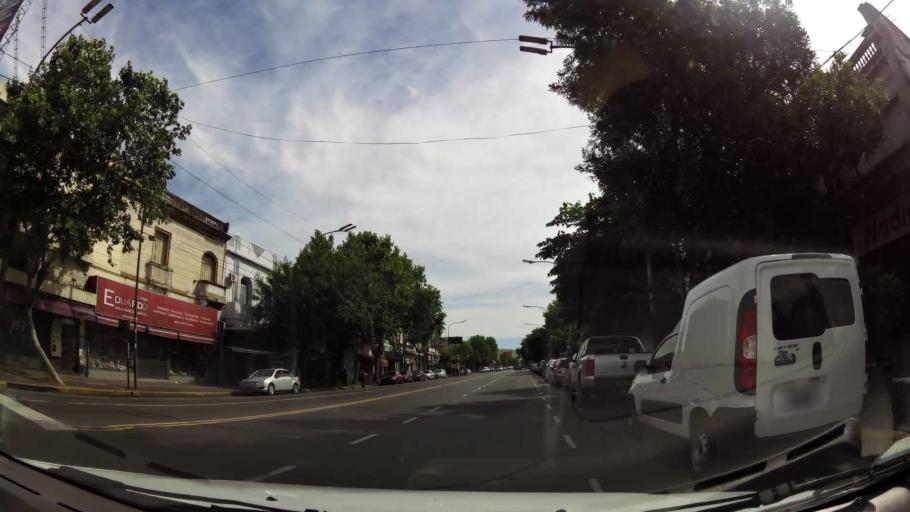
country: AR
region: Buenos Aires F.D.
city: Villa Lugano
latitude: -34.6537
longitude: -58.5048
